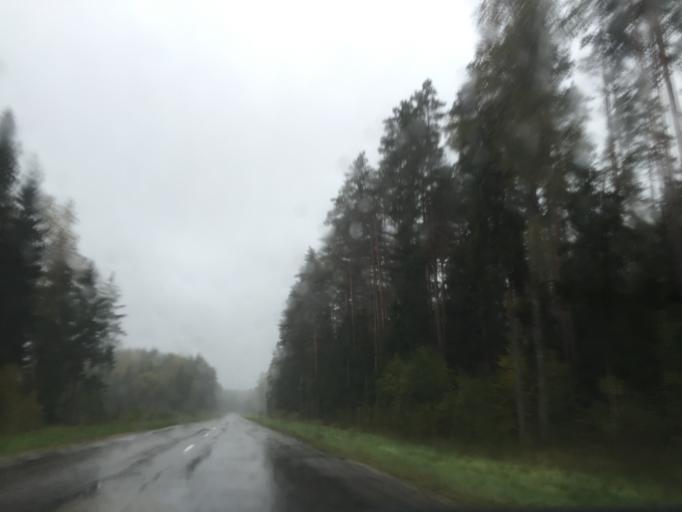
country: LV
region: Ropazu
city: Ropazi
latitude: 57.0166
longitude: 24.6825
